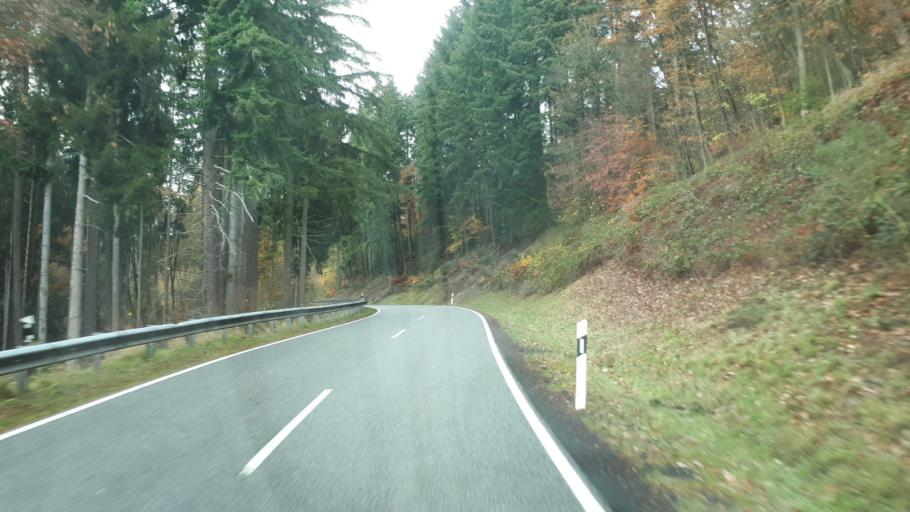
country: DE
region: Rheinland-Pfalz
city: Leienkaul
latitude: 50.1961
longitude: 7.0907
